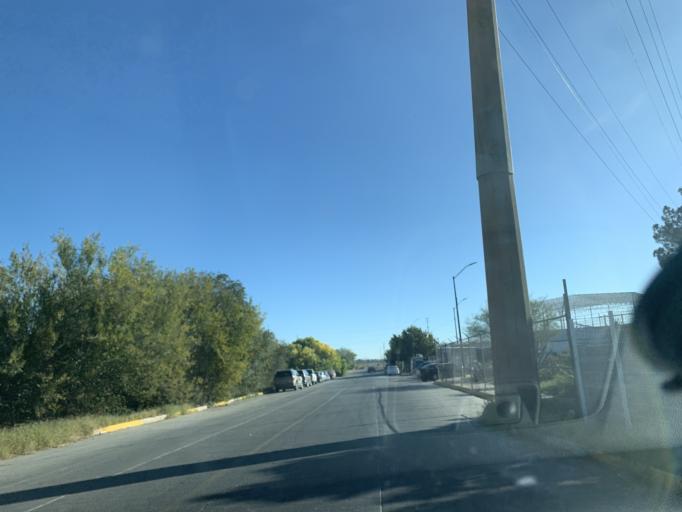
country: US
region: Texas
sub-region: El Paso County
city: Socorro
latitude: 31.7085
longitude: -106.3788
